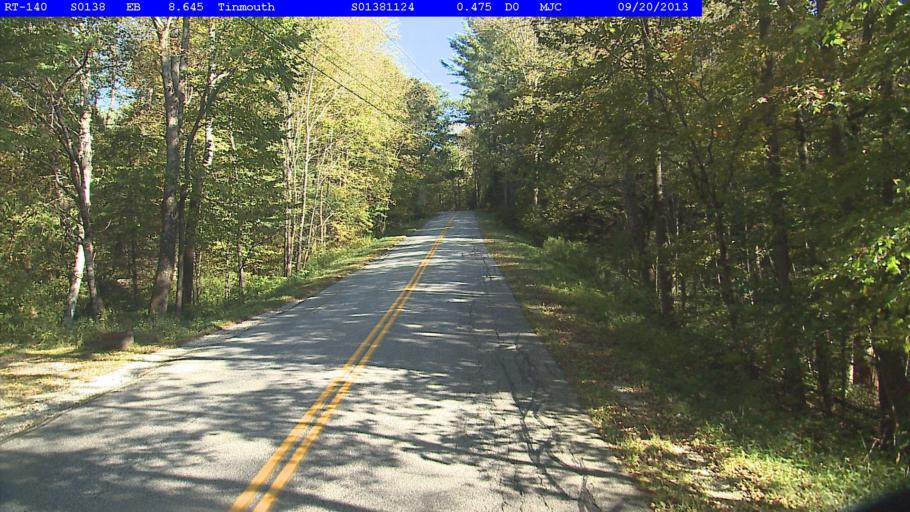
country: US
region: Vermont
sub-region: Rutland County
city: West Rutland
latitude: 43.4787
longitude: -73.0700
